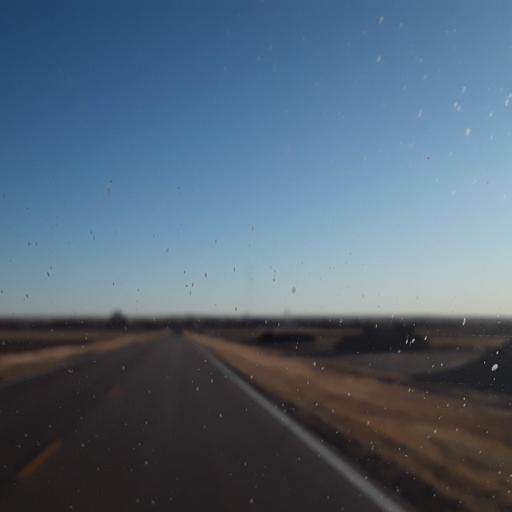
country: US
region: Kansas
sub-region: Wallace County
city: Sharon Springs
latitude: 38.9157
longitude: -101.7496
